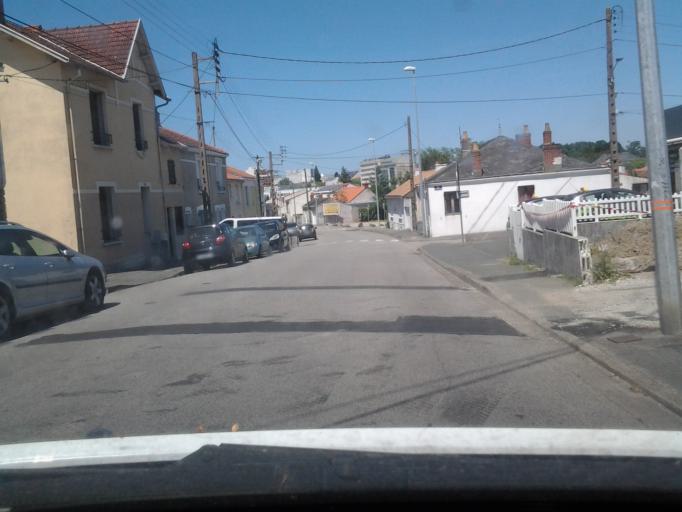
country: FR
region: Pays de la Loire
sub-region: Departement de la Vendee
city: La Roche-sur-Yon
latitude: 46.6612
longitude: -1.4309
